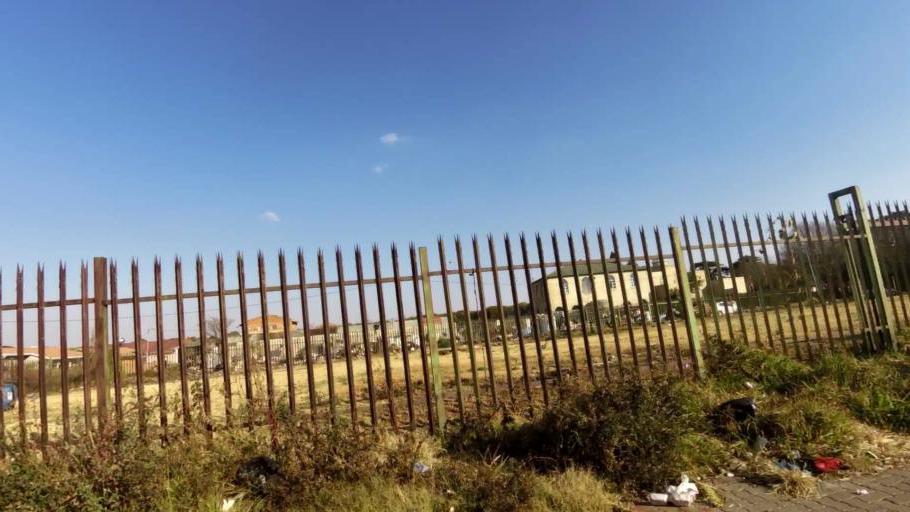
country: ZA
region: Gauteng
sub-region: City of Johannesburg Metropolitan Municipality
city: Johannesburg
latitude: -26.1966
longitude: 28.0160
